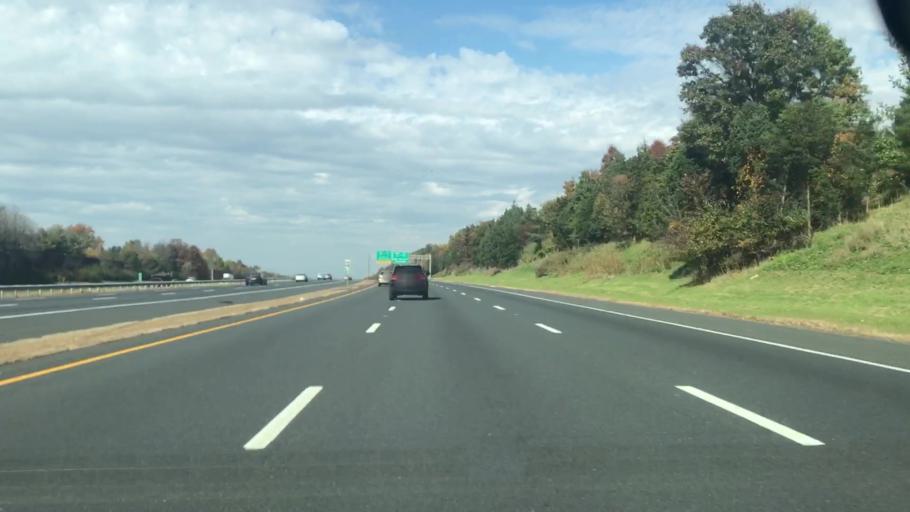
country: US
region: New Jersey
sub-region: Somerset County
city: Bridgewater
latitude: 40.6099
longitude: -74.6303
